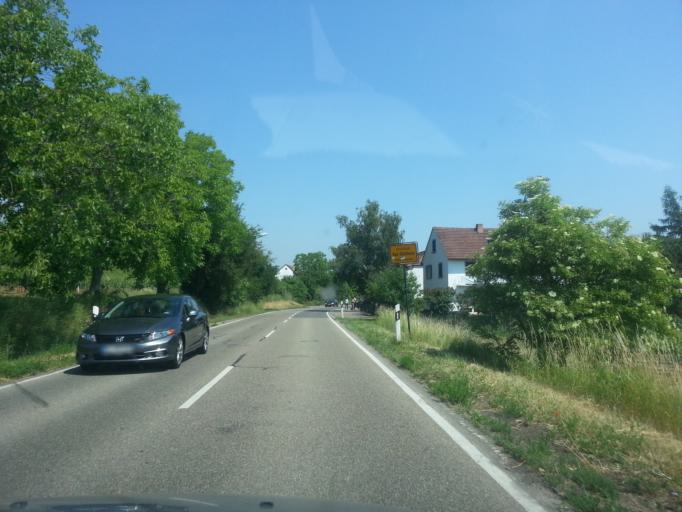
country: DE
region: Rheinland-Pfalz
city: Bad Duerkheim
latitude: 49.4742
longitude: 8.1755
